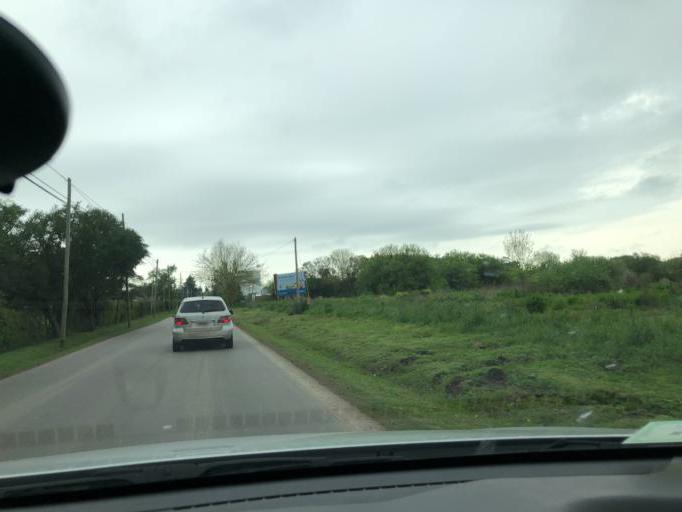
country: AR
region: Buenos Aires
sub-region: Partido de La Plata
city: La Plata
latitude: -34.8981
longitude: -58.0676
